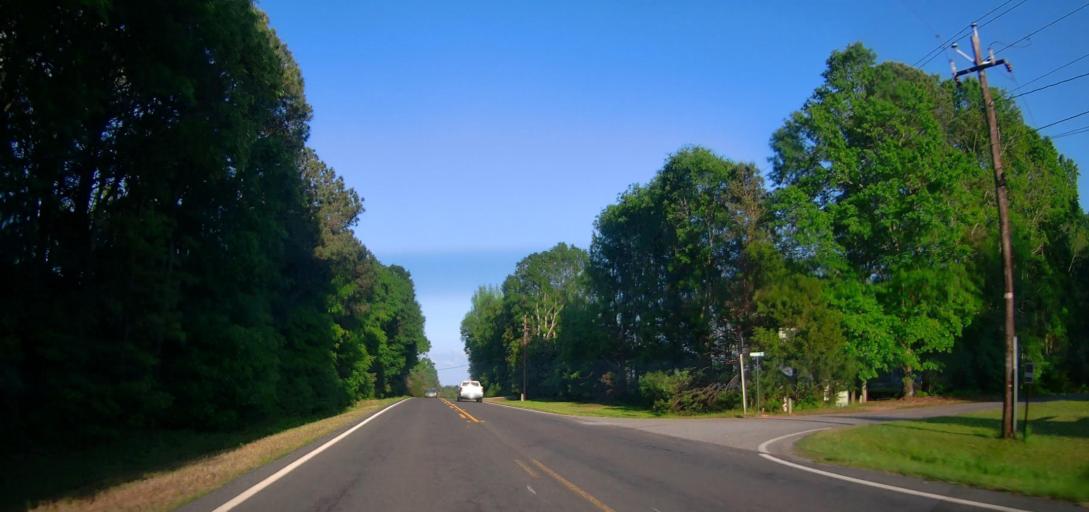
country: US
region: Georgia
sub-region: Walton County
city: Social Circle
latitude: 33.5086
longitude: -83.6715
